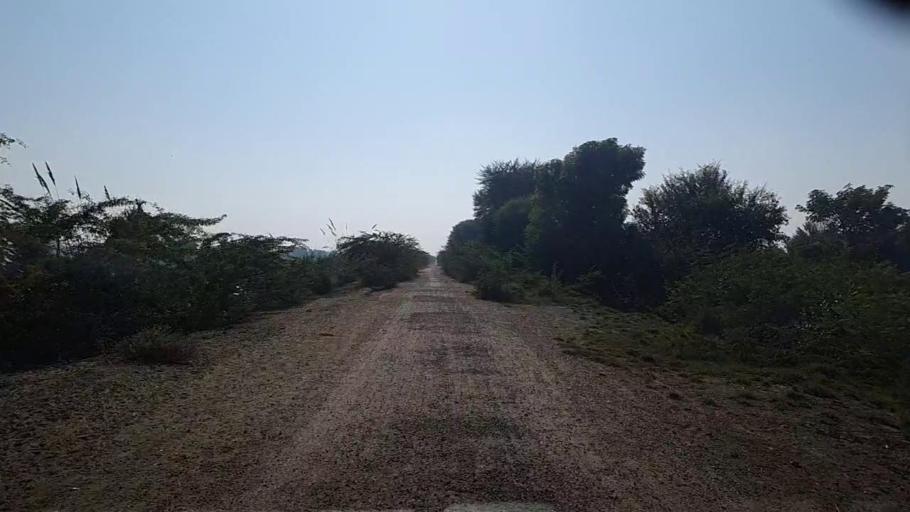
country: PK
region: Sindh
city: Pad Idan
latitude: 26.7839
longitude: 68.3362
